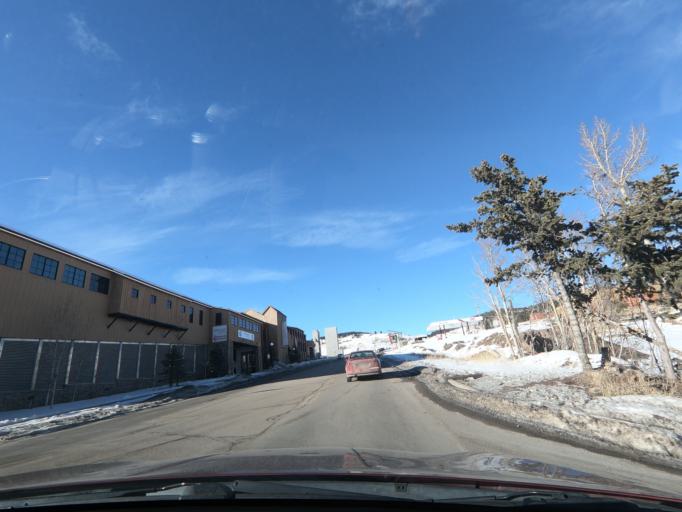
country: US
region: Colorado
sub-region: Teller County
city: Cripple Creek
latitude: 38.7496
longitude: -105.1730
